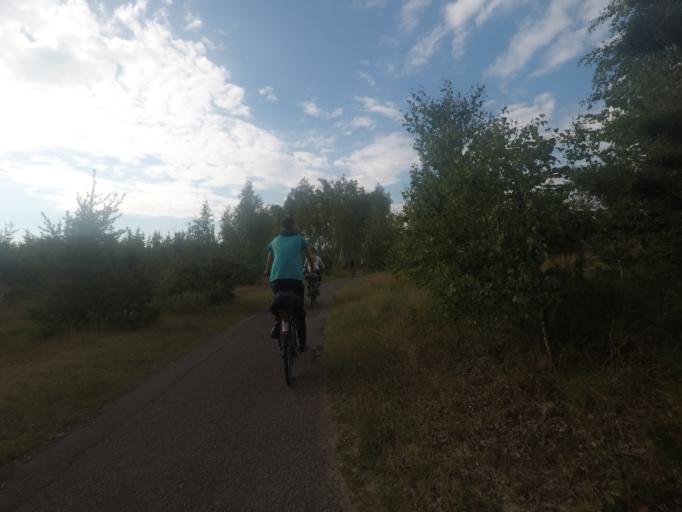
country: LT
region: Klaipedos apskritis
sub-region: Klaipeda
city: Klaipeda
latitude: 55.6314
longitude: 21.1169
